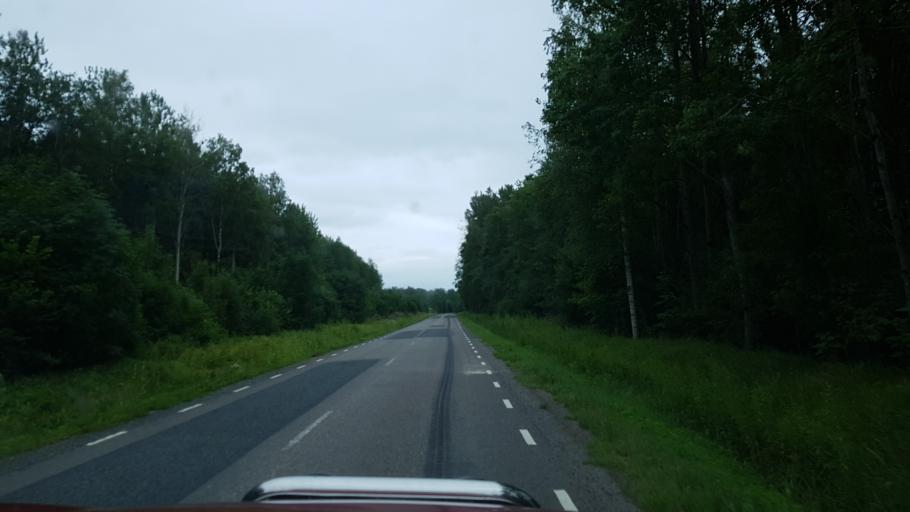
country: EE
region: Ida-Virumaa
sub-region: Johvi vald
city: Johvi
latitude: 59.4202
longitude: 27.4072
